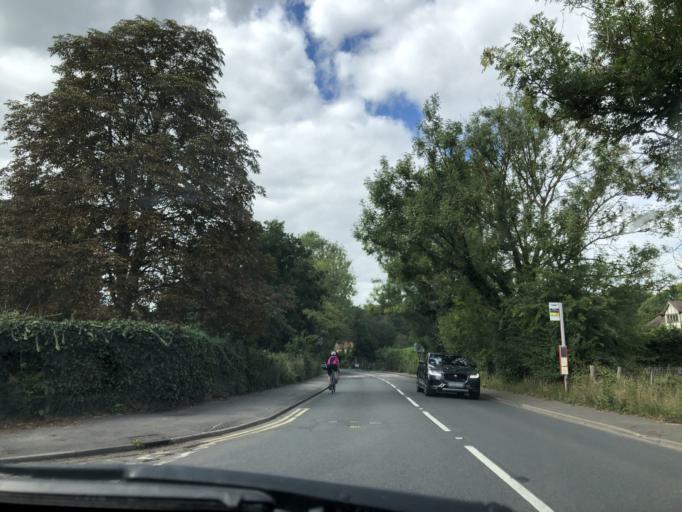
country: GB
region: England
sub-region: Kent
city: Westerham
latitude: 51.2780
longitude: 0.1192
